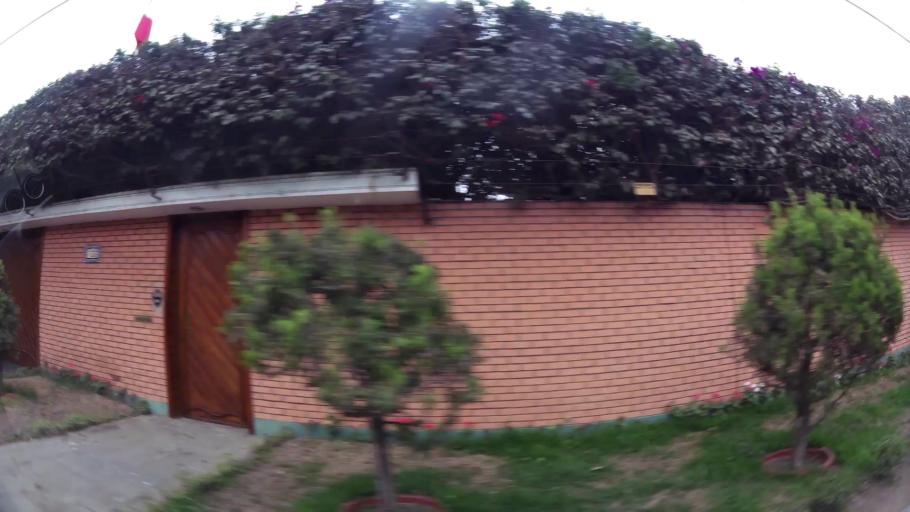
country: PE
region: Lima
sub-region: Lima
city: La Molina
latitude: -12.1024
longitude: -76.9754
